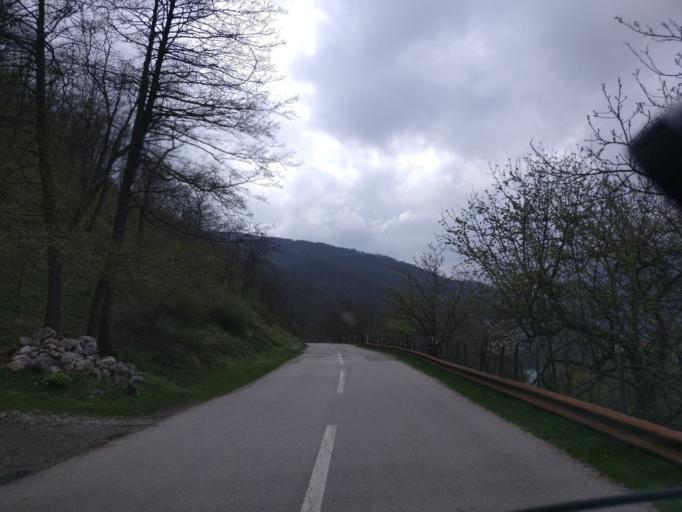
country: BA
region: Republika Srpska
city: Foca
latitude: 43.4803
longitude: 18.7483
